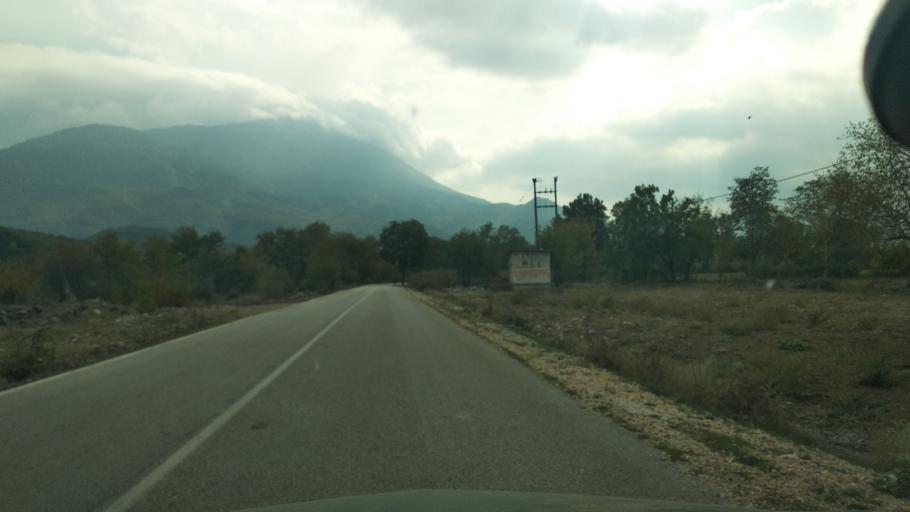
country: GR
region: Thessaly
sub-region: Trikala
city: Kastraki
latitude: 39.7054
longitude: 21.5263
